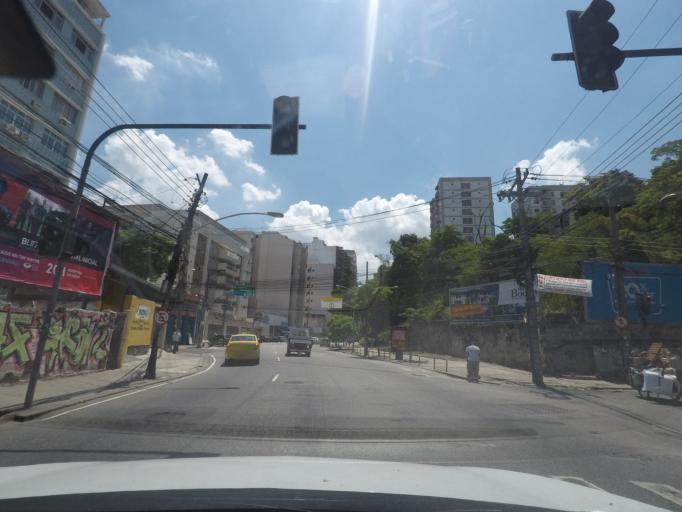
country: BR
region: Rio de Janeiro
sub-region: Rio De Janeiro
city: Rio de Janeiro
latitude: -22.9166
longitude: -43.2541
